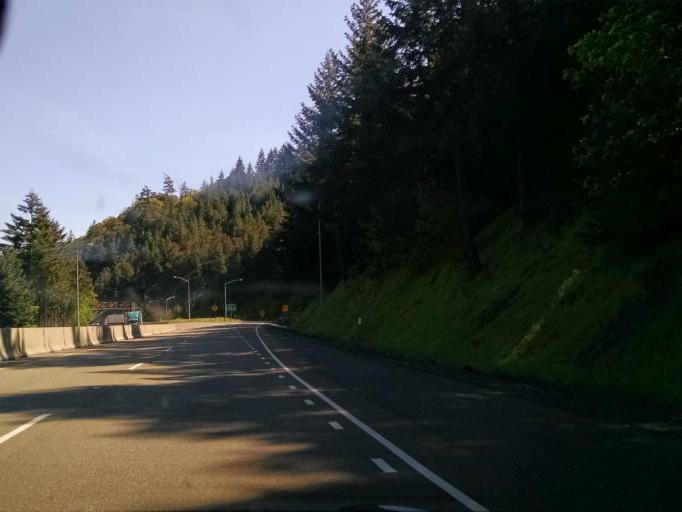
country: US
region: Oregon
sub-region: Douglas County
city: Myrtle Creek
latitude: 43.0283
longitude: -123.3012
